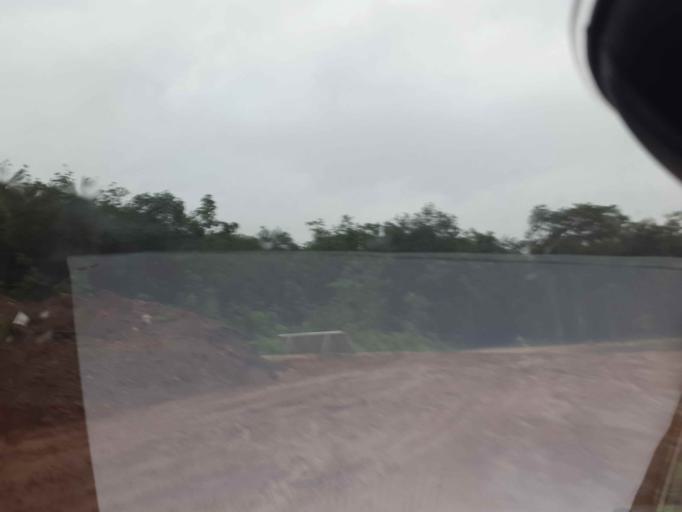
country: ID
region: Lampung
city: Panjang
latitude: -5.3930
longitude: 105.3463
